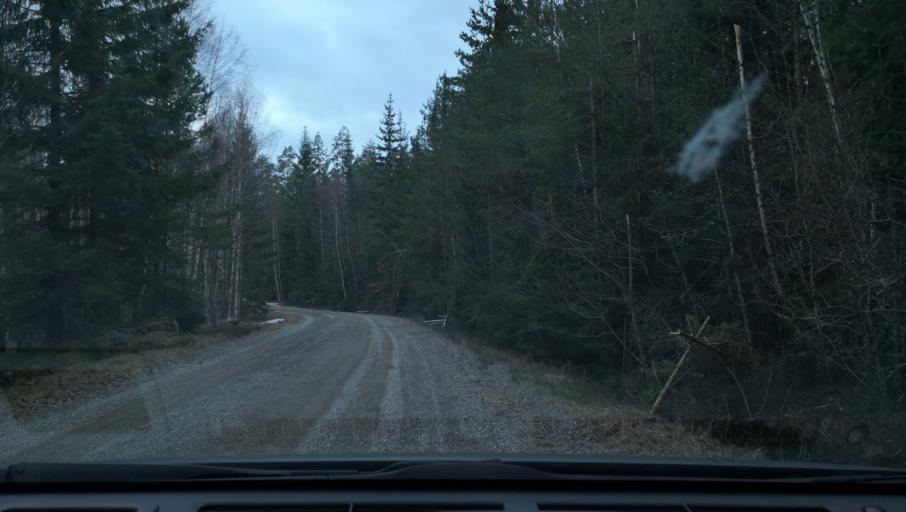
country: SE
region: Vaestmanland
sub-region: Kopings Kommun
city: Kolsva
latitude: 59.5654
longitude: 15.7977
